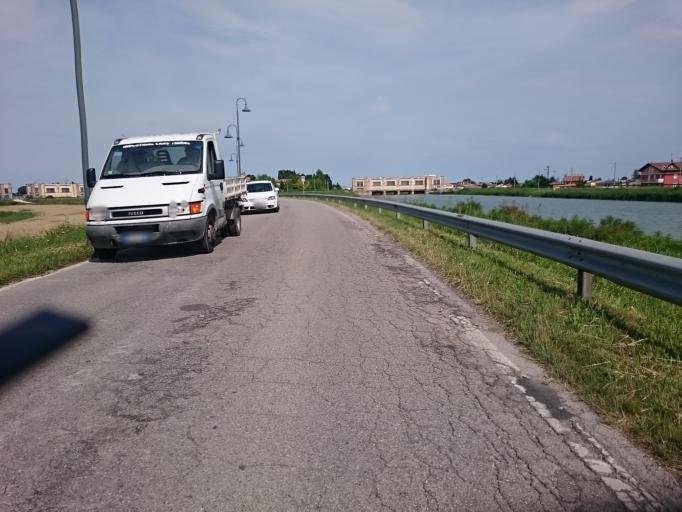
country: IT
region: Veneto
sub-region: Provincia di Padova
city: Ponte San Nicolo
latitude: 45.3842
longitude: 11.9010
